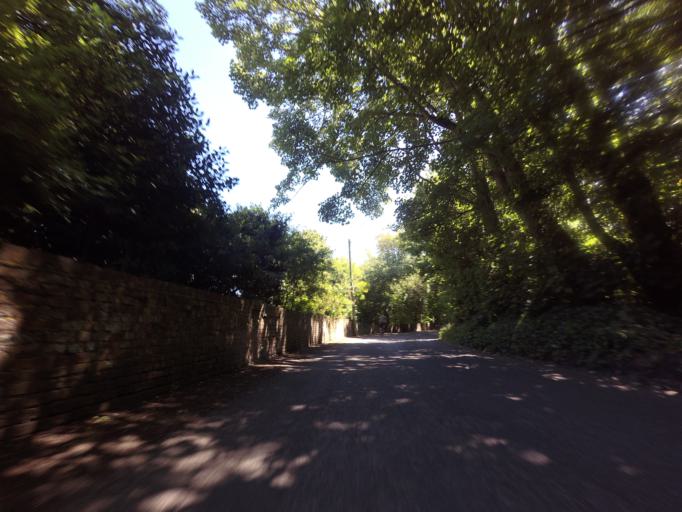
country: GB
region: England
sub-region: Kent
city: Deal
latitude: 51.1987
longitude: 1.3632
